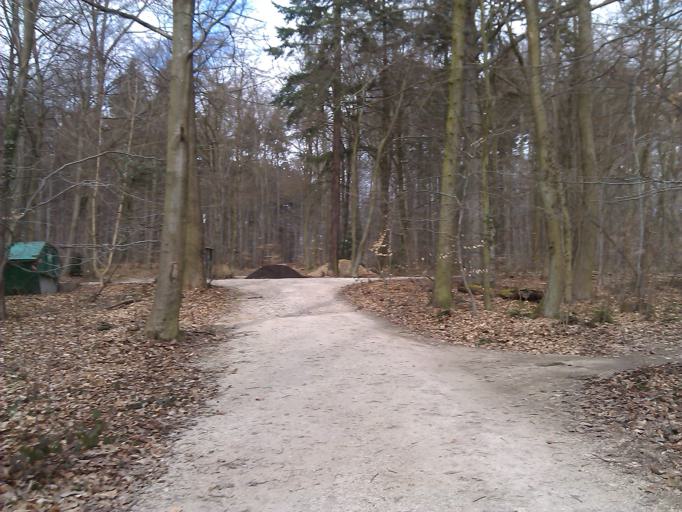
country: DE
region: Rheinland-Pfalz
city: Bingen am Rhein
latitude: 49.9814
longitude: 7.8982
